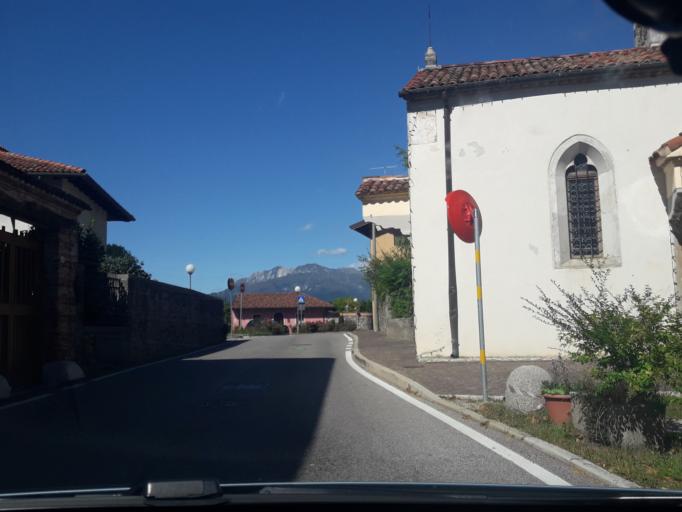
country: IT
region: Friuli Venezia Giulia
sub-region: Provincia di Udine
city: Tricesimo
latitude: 46.1500
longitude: 13.2155
